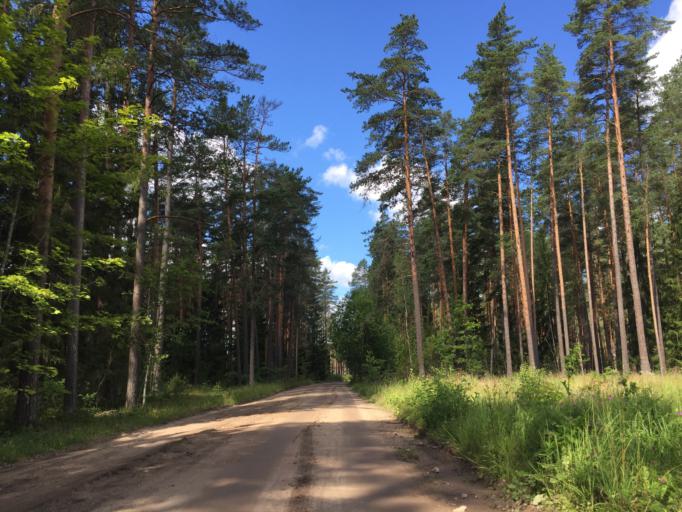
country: LV
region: Garkalne
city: Garkalne
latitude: 56.9712
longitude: 24.4703
